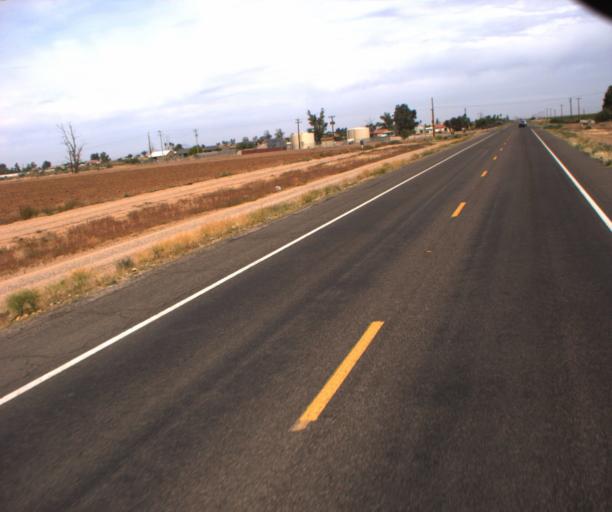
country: US
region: Arizona
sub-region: Pinal County
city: Eloy
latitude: 32.7763
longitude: -111.5155
